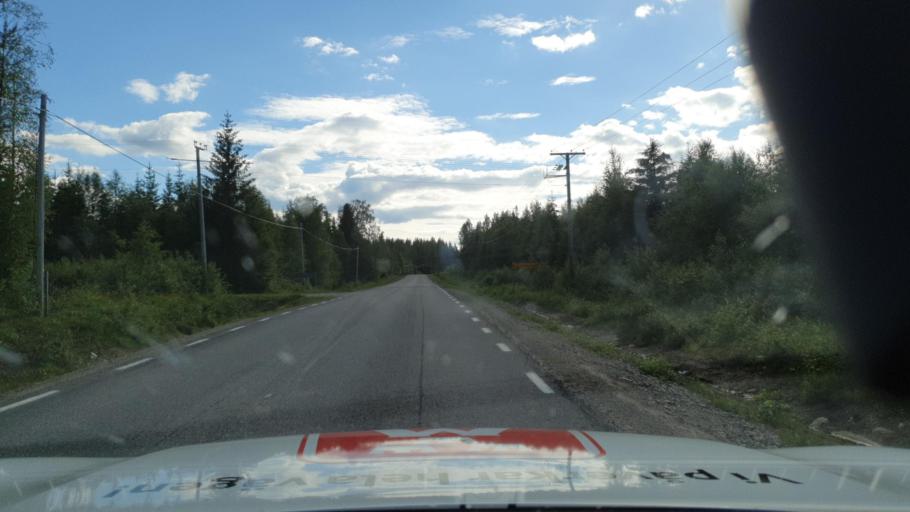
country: SE
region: Vaesterbotten
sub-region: Skelleftea Kommun
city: Langsele
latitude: 64.7676
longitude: 19.9967
